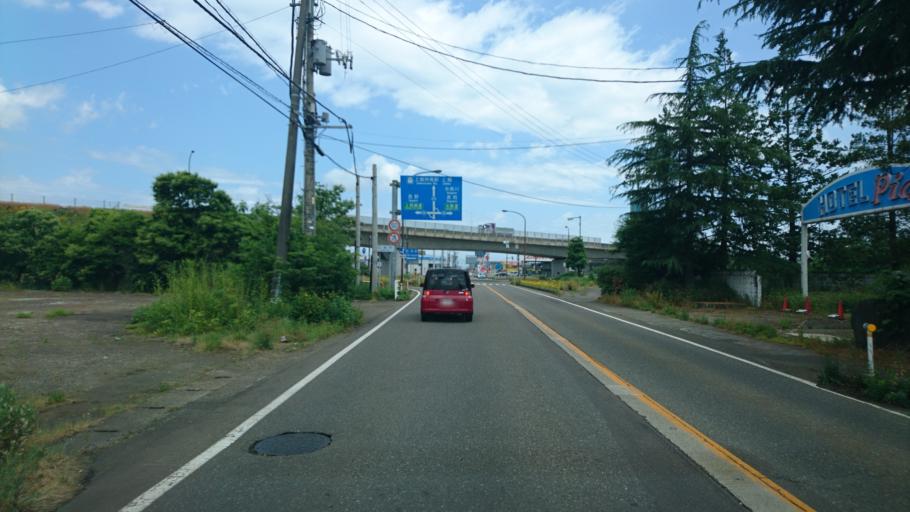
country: JP
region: Niigata
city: Arai
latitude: 37.0588
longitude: 138.2598
